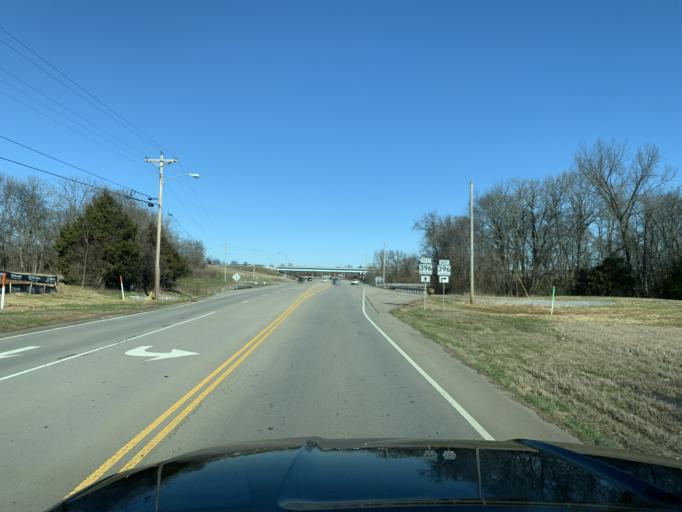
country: US
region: Tennessee
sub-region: Maury County
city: Spring Hill
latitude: 35.7292
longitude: -86.9245
